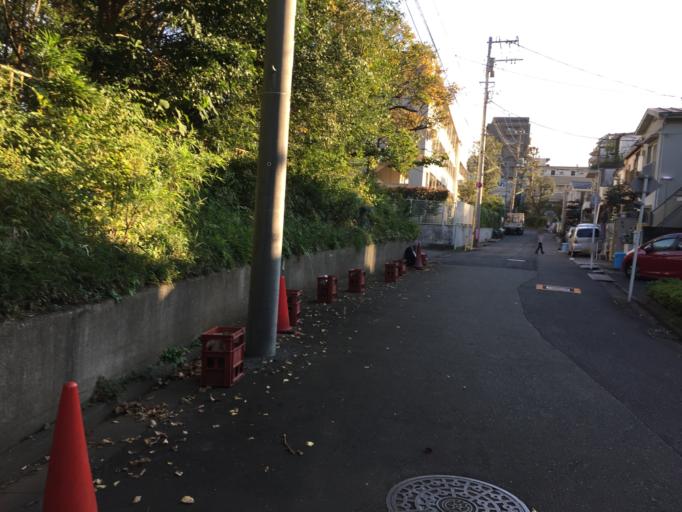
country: JP
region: Tokyo
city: Tokyo
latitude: 35.6320
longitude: 139.6524
